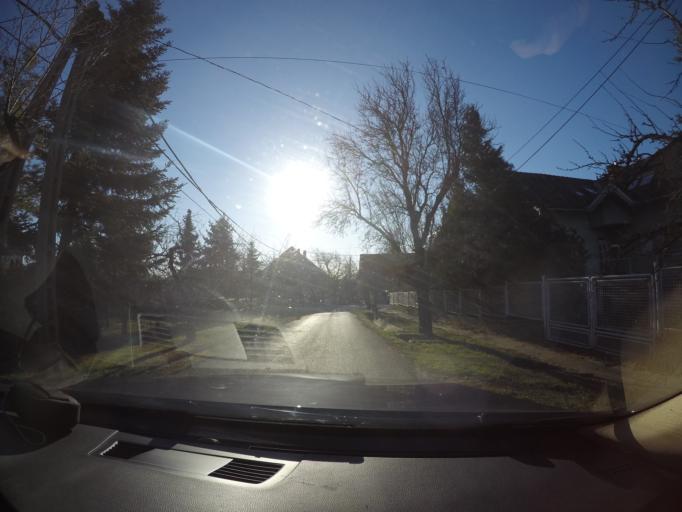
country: HU
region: Pest
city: Budaors
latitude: 47.4644
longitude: 18.9778
